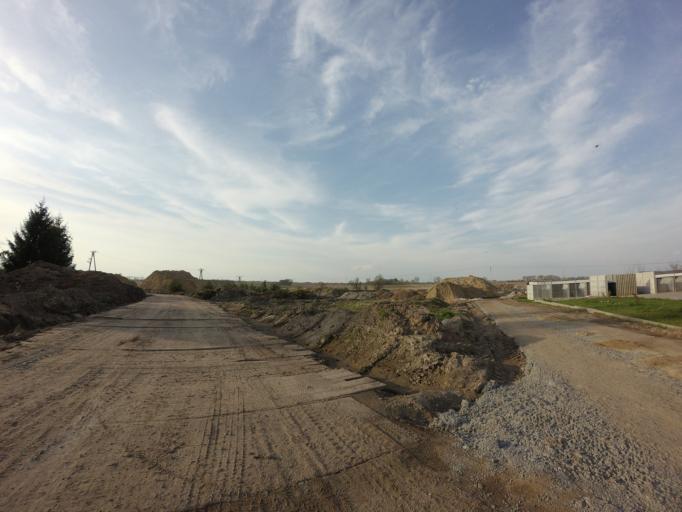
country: PL
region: West Pomeranian Voivodeship
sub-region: Powiat choszczenski
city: Choszczno
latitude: 53.1723
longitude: 15.4473
